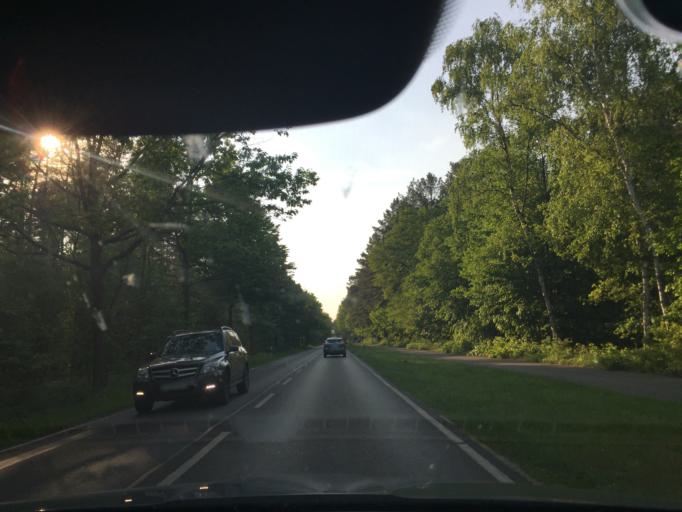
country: DE
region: Berlin
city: Grunau
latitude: 52.4027
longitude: 13.5953
